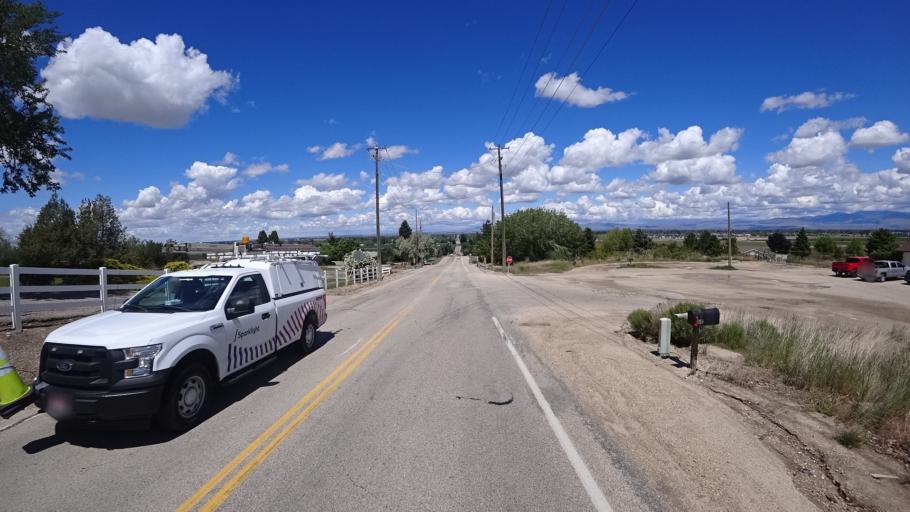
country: US
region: Idaho
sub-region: Ada County
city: Meridian
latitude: 43.5925
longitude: -116.4536
